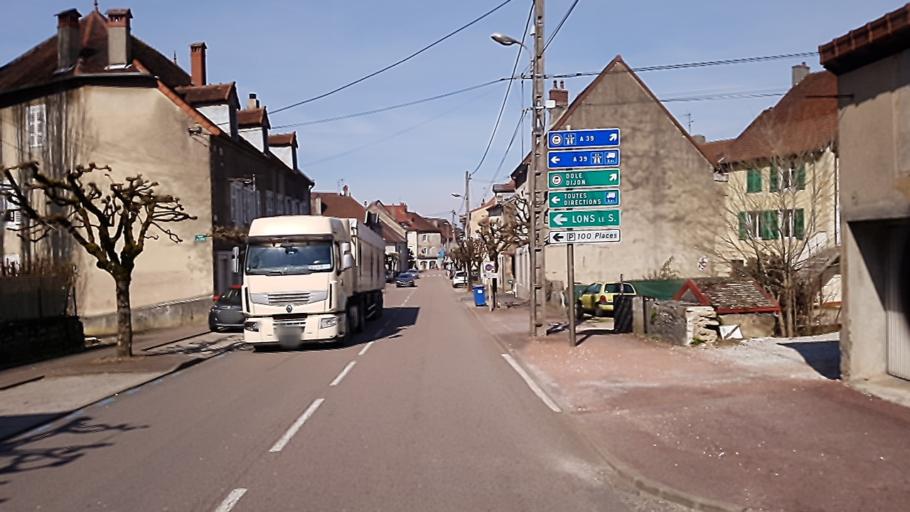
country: FR
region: Franche-Comte
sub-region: Departement du Jura
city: Poligny
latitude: 46.8331
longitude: 5.7106
